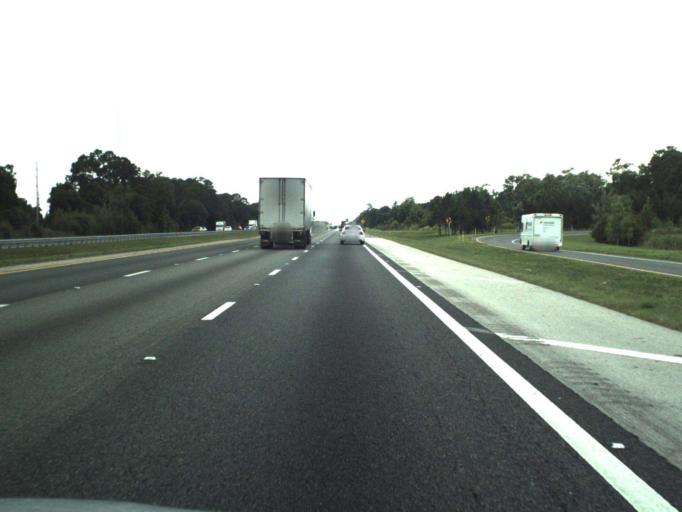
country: US
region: Florida
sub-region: Volusia County
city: Lake Helen
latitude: 28.9843
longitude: -81.2487
